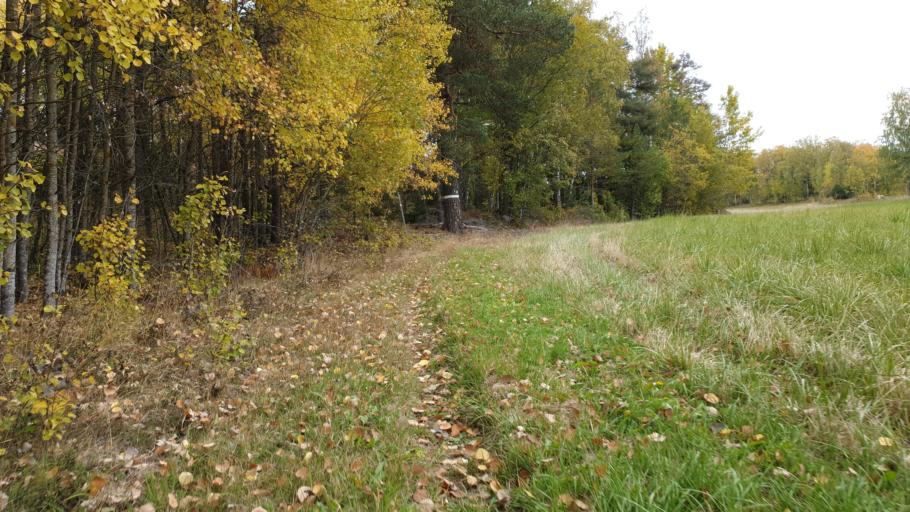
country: SE
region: Vaestmanland
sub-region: Sala Kommun
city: Sala
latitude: 59.8151
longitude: 16.6510
